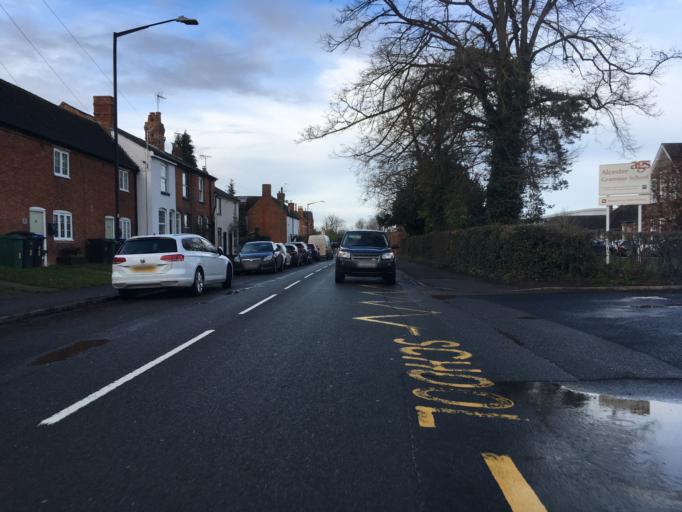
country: GB
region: England
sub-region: Warwickshire
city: Alcester
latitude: 52.2177
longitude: -1.8757
